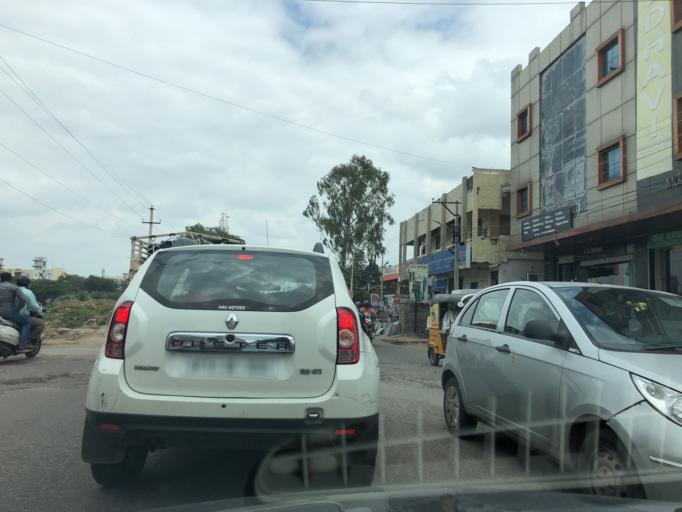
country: IN
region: Telangana
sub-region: Rangareddi
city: Quthbullapur
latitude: 17.4689
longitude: 78.4786
